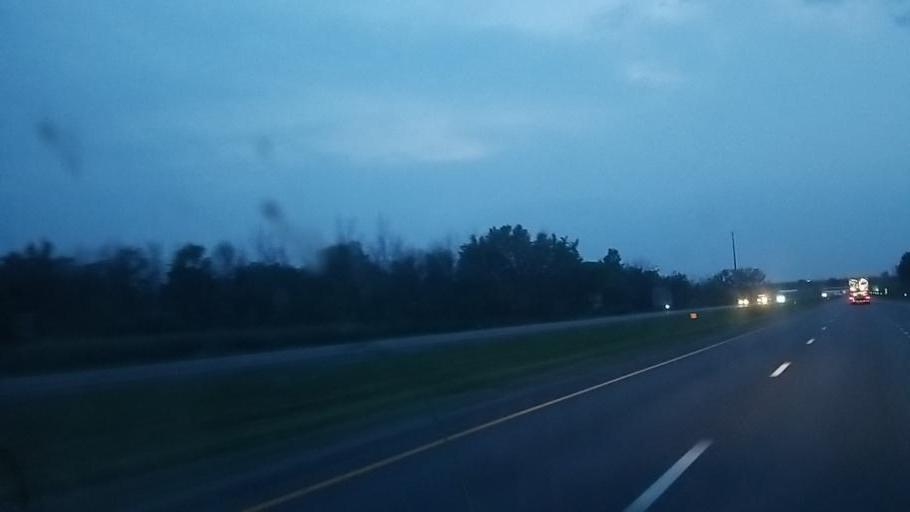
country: US
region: New York
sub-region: Onondaga County
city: East Syracuse
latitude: 43.0948
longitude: -76.0491
